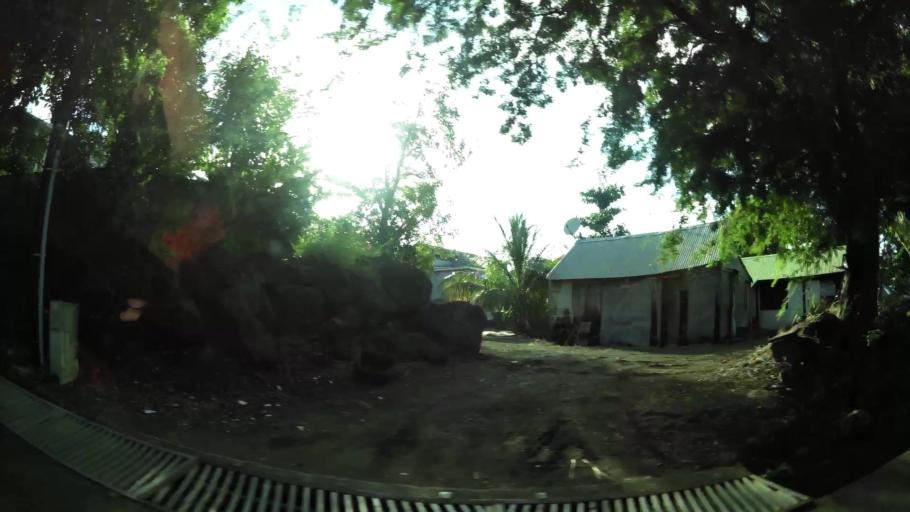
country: GP
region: Guadeloupe
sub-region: Guadeloupe
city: Pointe-Noire
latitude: 16.1919
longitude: -61.7794
